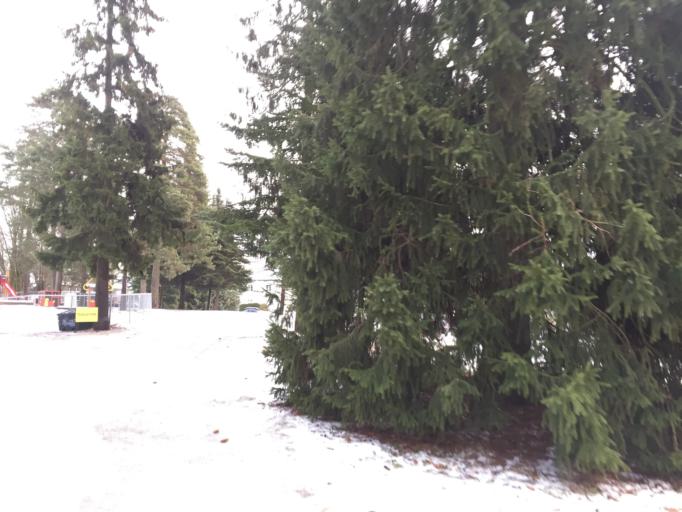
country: NO
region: Oslo
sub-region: Oslo
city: Sjolyststranda
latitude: 59.9479
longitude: 10.7019
